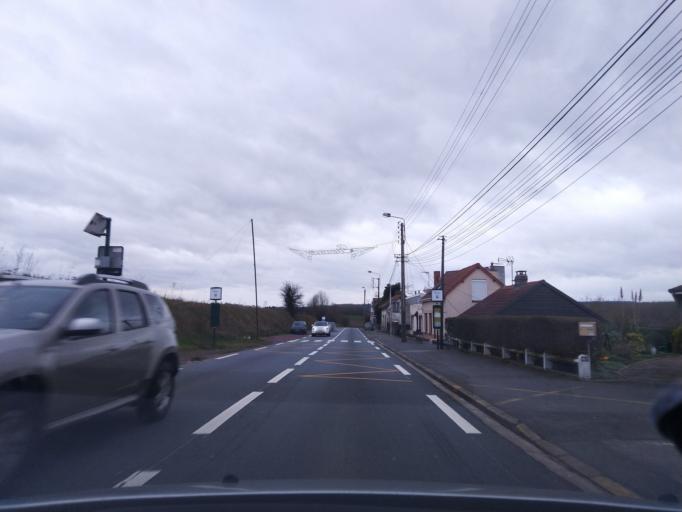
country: FR
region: Nord-Pas-de-Calais
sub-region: Departement du Pas-de-Calais
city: Divion
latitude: 50.4649
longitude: 2.4962
